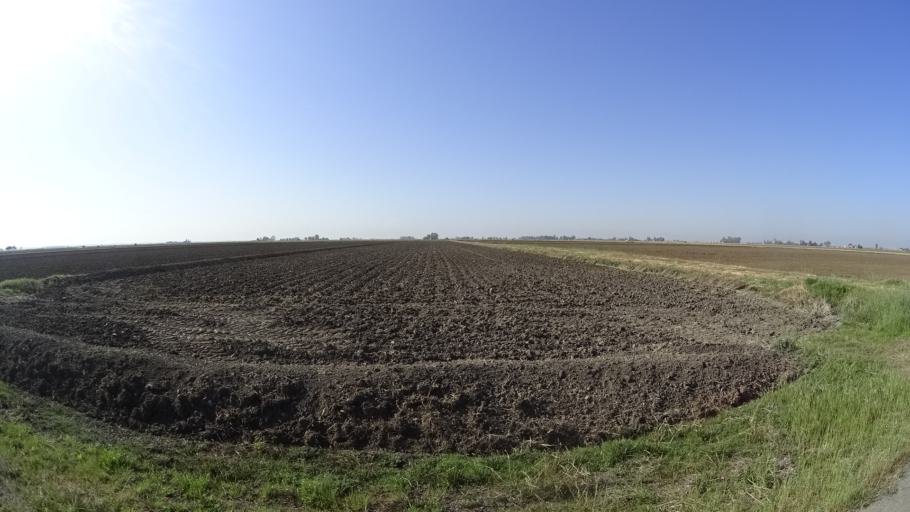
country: US
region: California
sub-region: Glenn County
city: Willows
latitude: 39.5726
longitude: -122.0908
